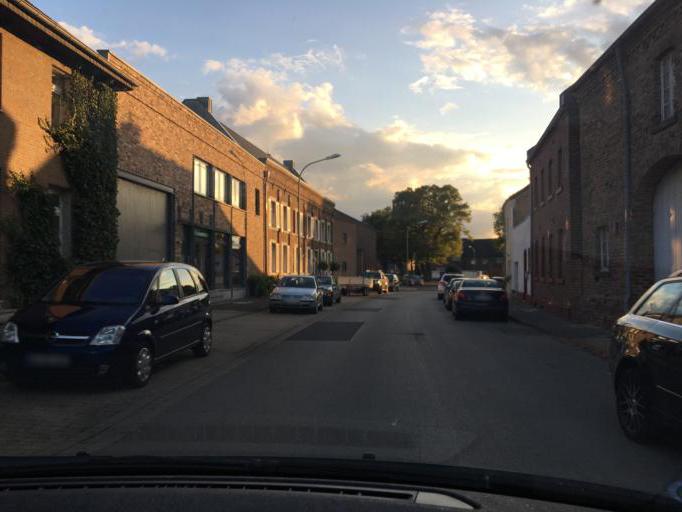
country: DE
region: North Rhine-Westphalia
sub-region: Regierungsbezirk Koln
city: Niederzier
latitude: 50.8842
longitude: 6.4669
